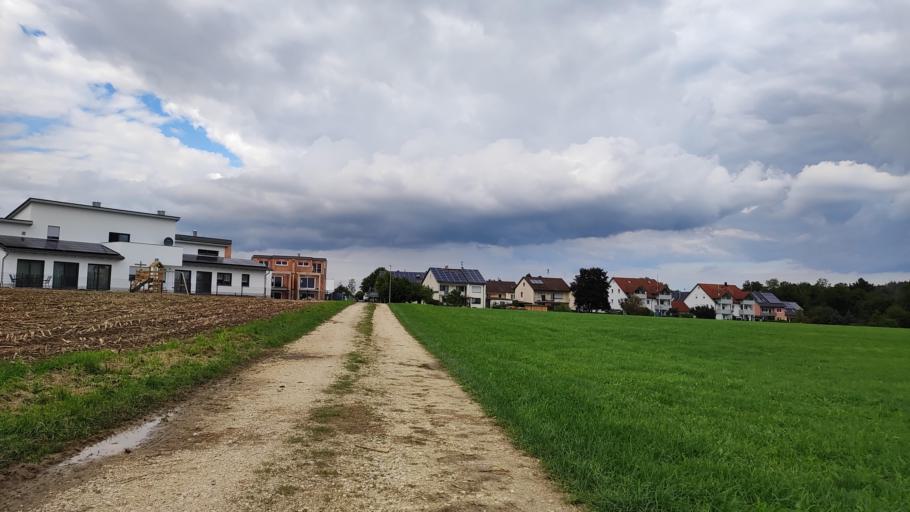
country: DE
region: Bavaria
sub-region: Swabia
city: Altenmunster
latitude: 48.4566
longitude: 10.5845
